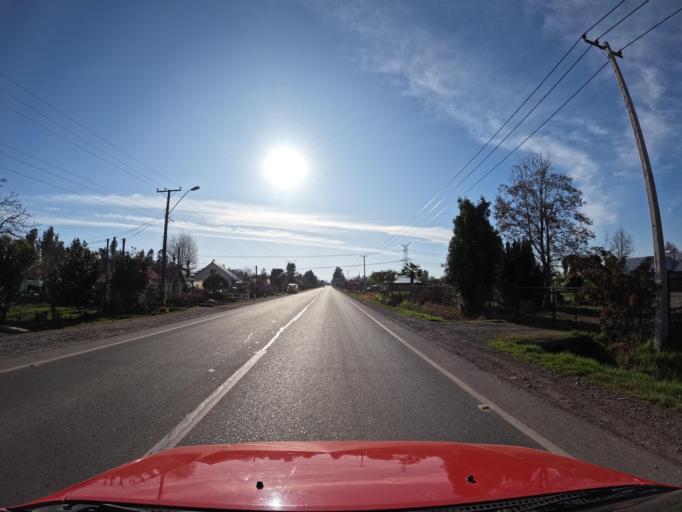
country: CL
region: Maule
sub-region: Provincia de Curico
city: Teno
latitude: -34.9463
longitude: -70.9944
